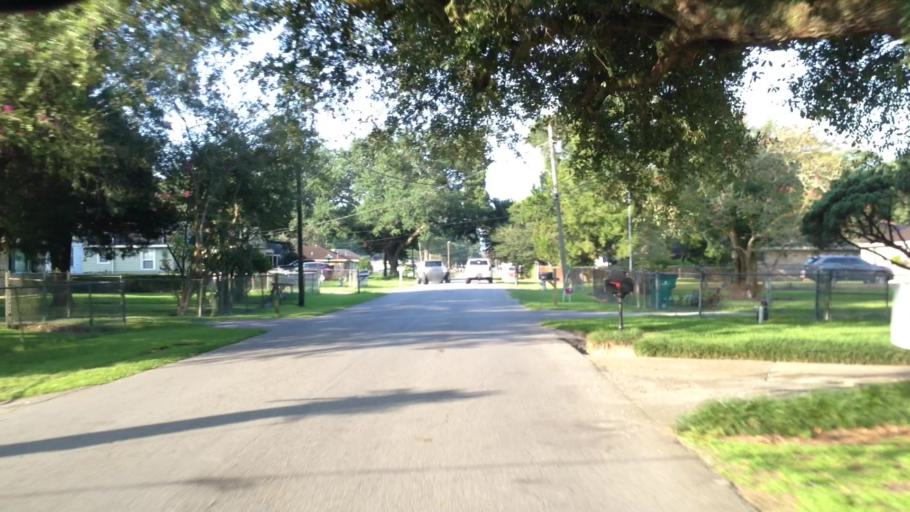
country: US
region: Louisiana
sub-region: Jefferson Parish
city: Bridge City
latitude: 29.9390
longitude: -90.1558
